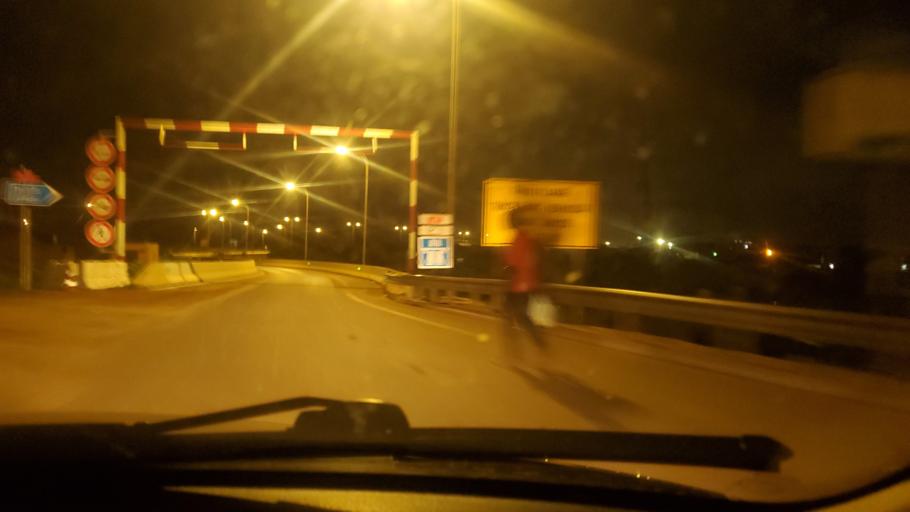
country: SN
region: Dakar
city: Pikine
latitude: 14.7481
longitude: -17.3769
